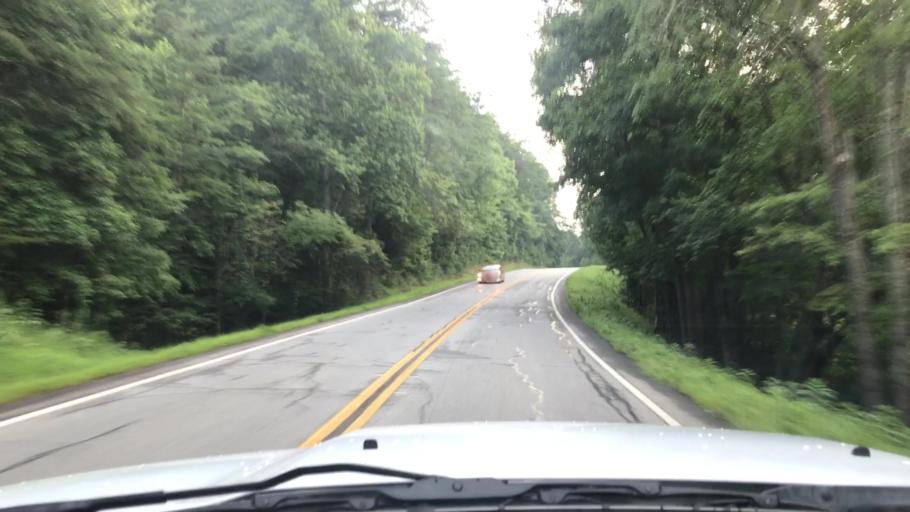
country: US
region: Georgia
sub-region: Fannin County
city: Blue Ridge
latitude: 34.9281
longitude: -84.2637
